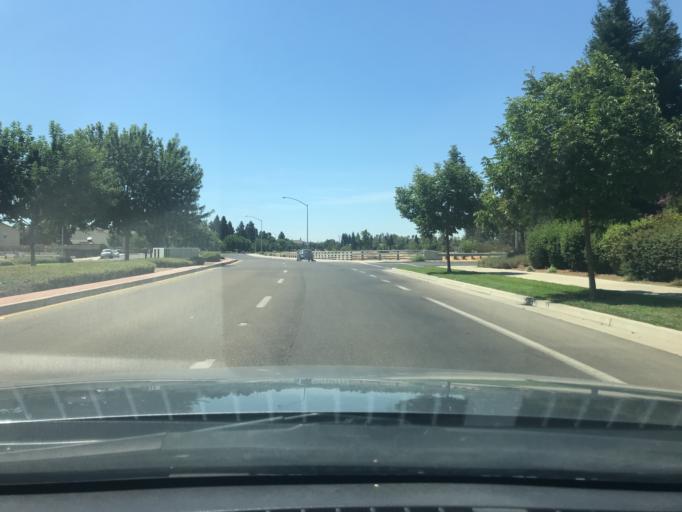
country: US
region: California
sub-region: Merced County
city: Merced
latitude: 37.3369
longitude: -120.4870
